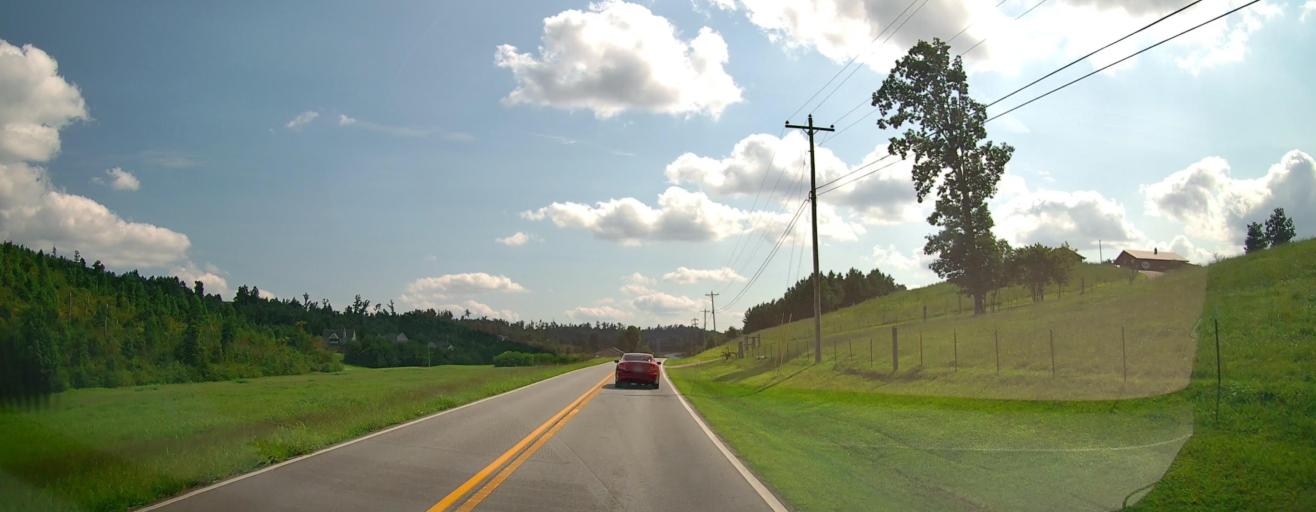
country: US
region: Georgia
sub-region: Catoosa County
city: Ringgold
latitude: 34.9679
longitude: -85.0682
